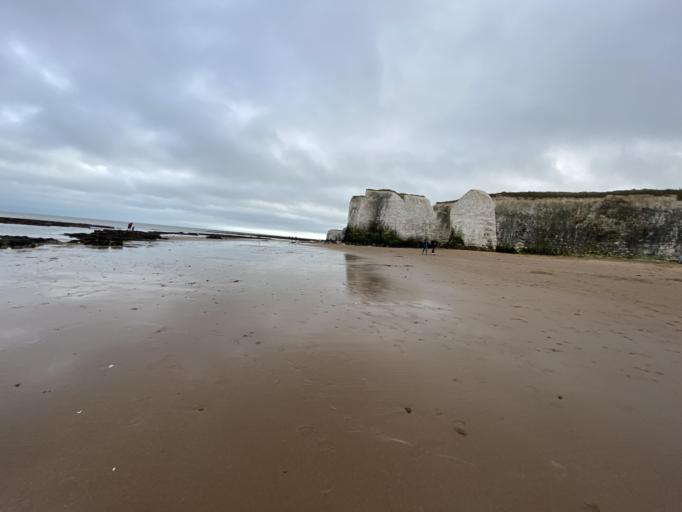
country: GB
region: England
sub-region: Kent
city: Broadstairs
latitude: 51.3893
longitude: 1.4362
